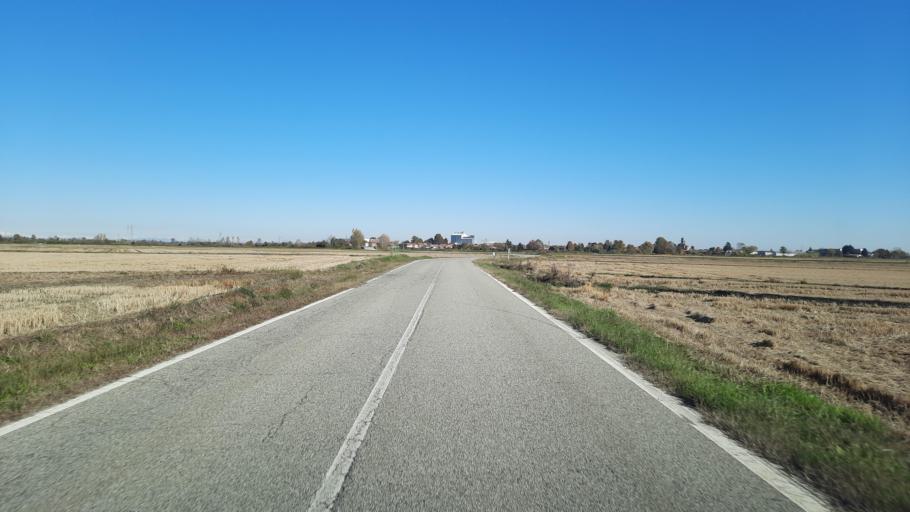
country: IT
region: Piedmont
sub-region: Provincia di Alessandria
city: Balzola
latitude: 45.1766
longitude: 8.3873
